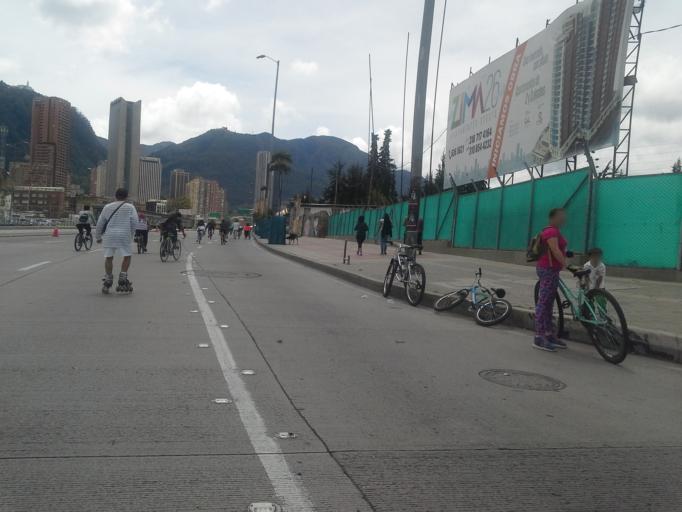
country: CO
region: Bogota D.C.
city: Bogota
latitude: 4.6216
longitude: -74.0775
